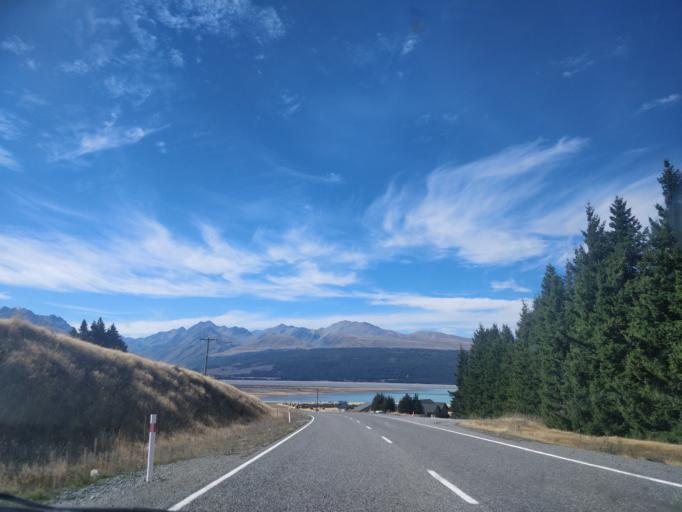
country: NZ
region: Canterbury
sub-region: Timaru District
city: Pleasant Point
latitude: -43.9129
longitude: 170.1186
